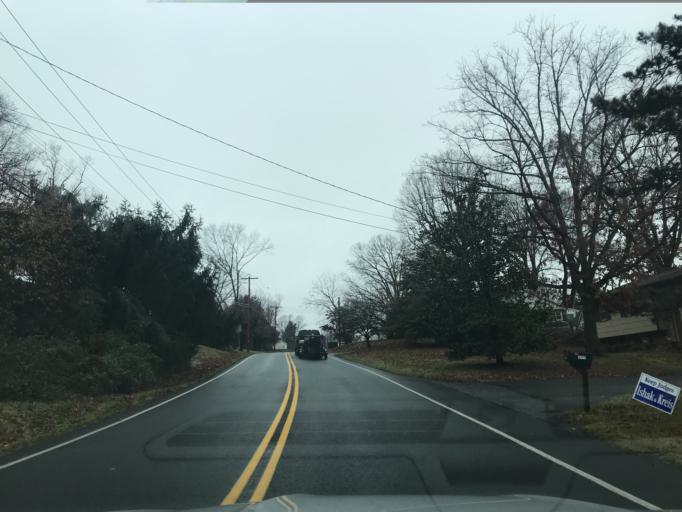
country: US
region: Maryland
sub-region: Harford County
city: South Bel Air
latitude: 39.5656
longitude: -76.3167
